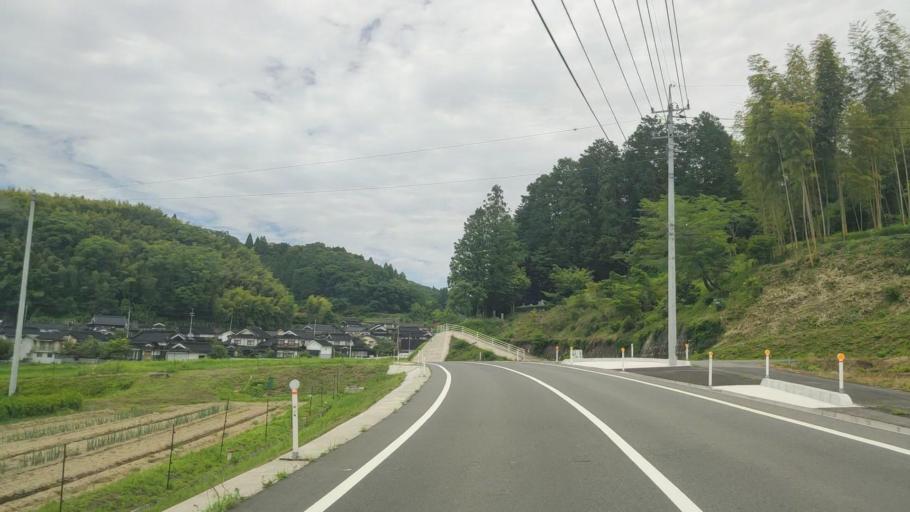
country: JP
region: Okayama
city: Tsuyama
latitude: 35.0671
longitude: 134.2353
